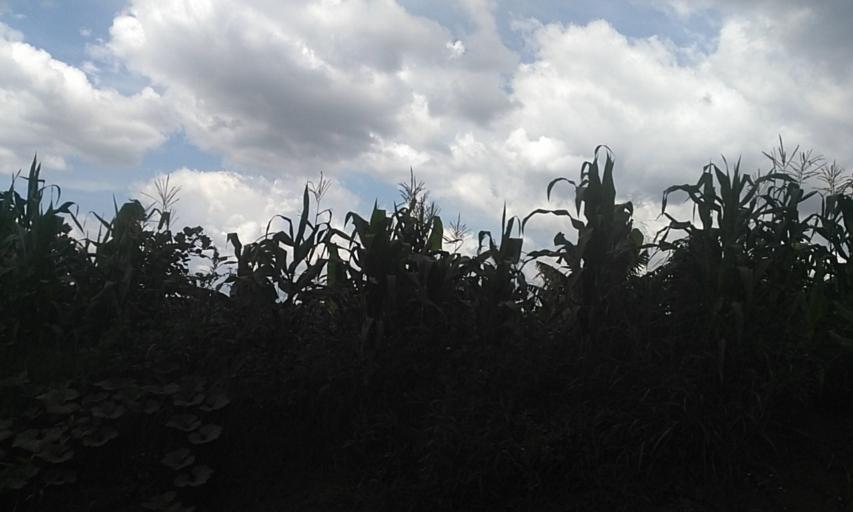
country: UG
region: Central Region
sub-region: Wakiso District
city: Wakiso
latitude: 0.3495
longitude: 32.4794
